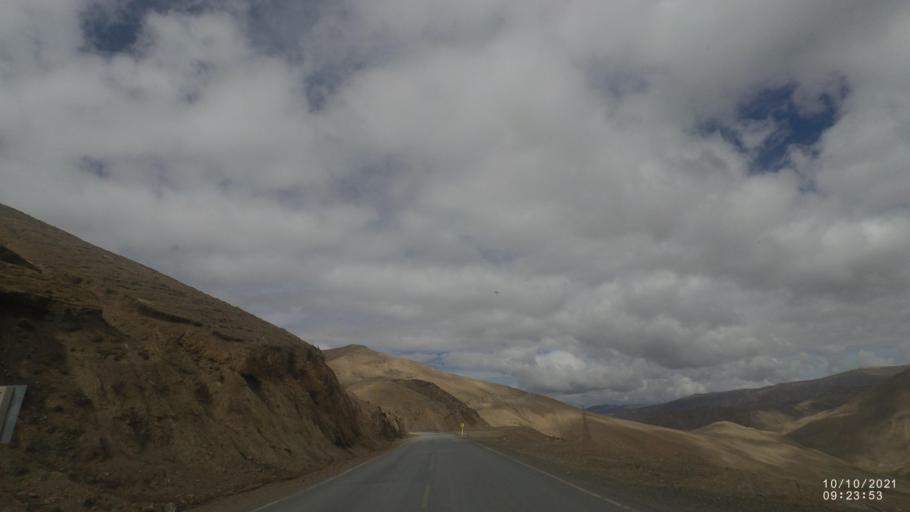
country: BO
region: La Paz
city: Quime
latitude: -17.0871
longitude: -67.3064
